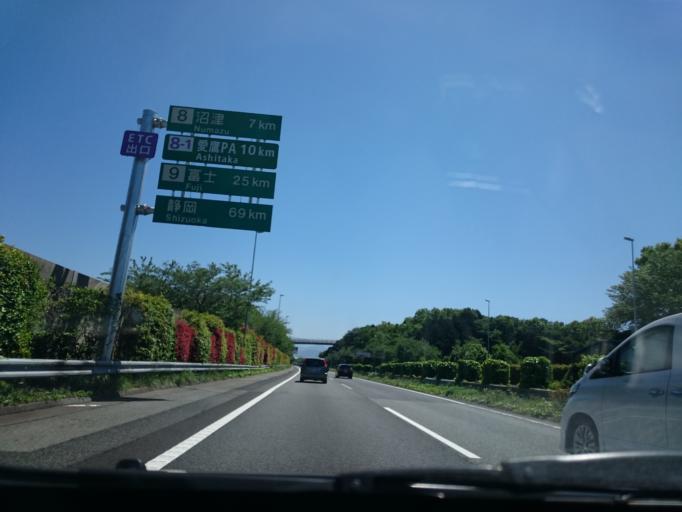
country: JP
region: Shizuoka
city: Mishima
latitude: 35.1986
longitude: 138.9027
